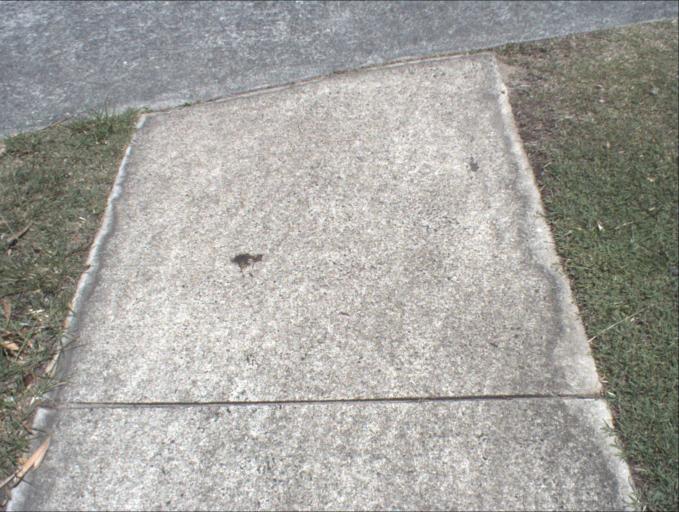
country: AU
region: Queensland
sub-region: Logan
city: Rochedale South
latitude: -27.6026
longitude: 153.1147
